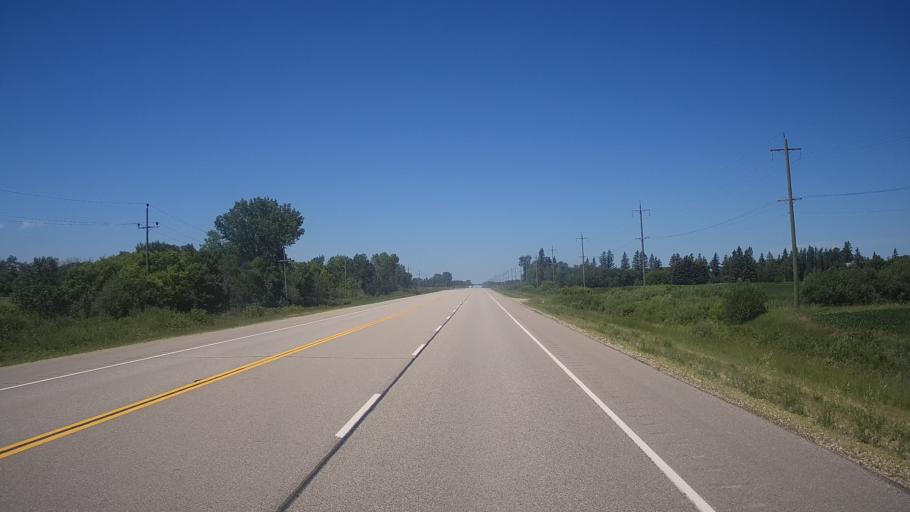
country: CA
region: Manitoba
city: Neepawa
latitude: 50.2249
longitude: -99.2781
